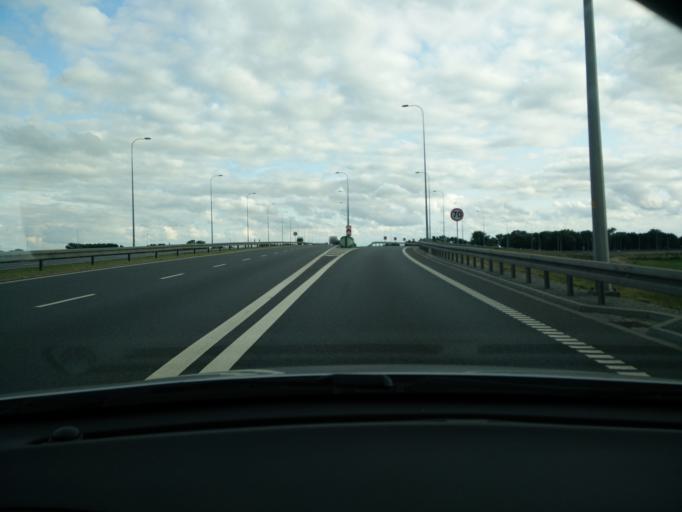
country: PL
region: Pomeranian Voivodeship
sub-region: Gdansk
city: Gdansk
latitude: 54.3218
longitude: 18.7051
